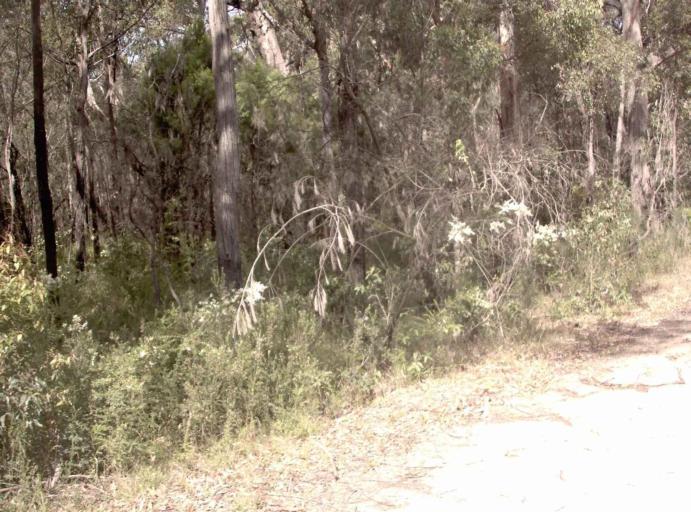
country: AU
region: New South Wales
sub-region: Bega Valley
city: Eden
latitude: -37.5565
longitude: 149.7467
